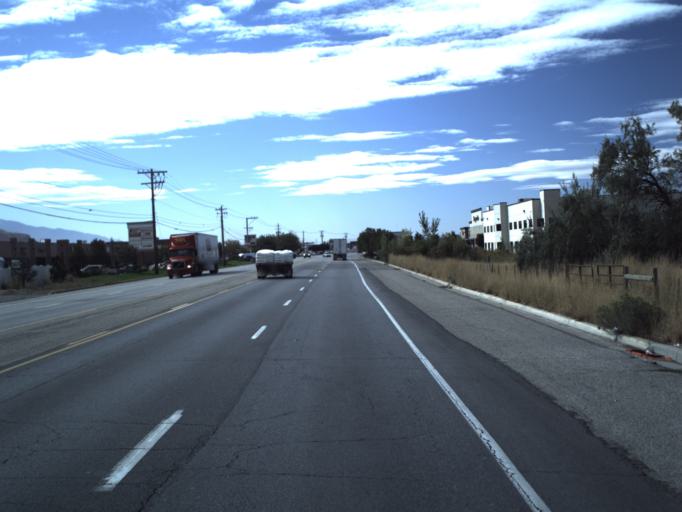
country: US
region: Utah
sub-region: Davis County
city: North Salt Lake
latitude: 40.8513
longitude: -111.9298
